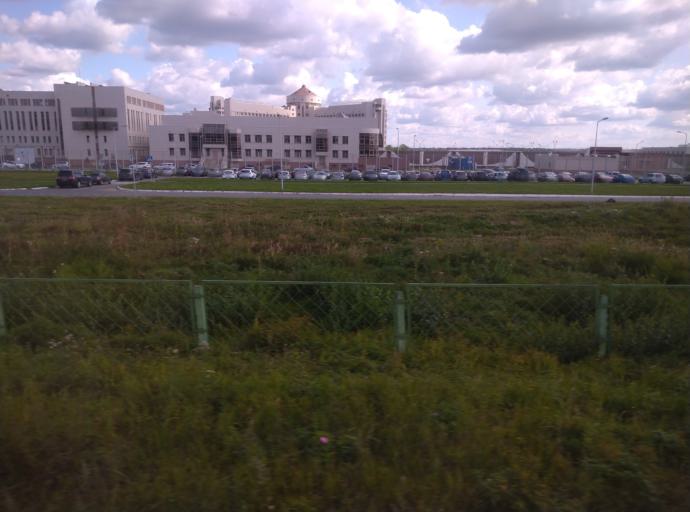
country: RU
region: St.-Petersburg
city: Kolpino
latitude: 59.7369
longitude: 30.6300
